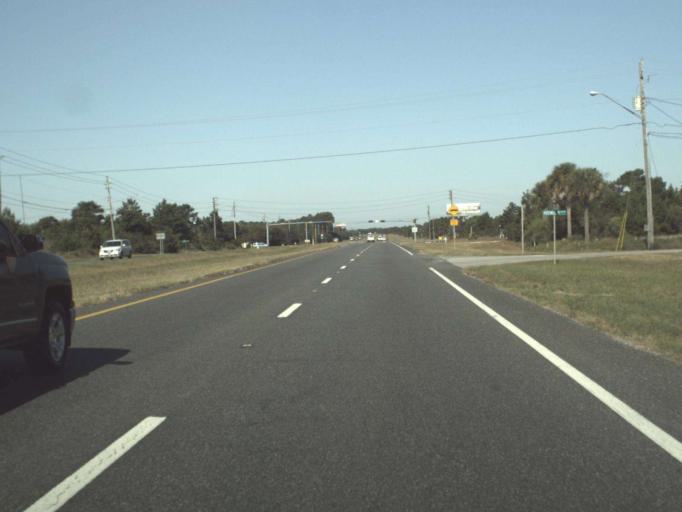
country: US
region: Florida
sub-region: Bay County
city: Laguna Beach
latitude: 30.2535
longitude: -85.9390
